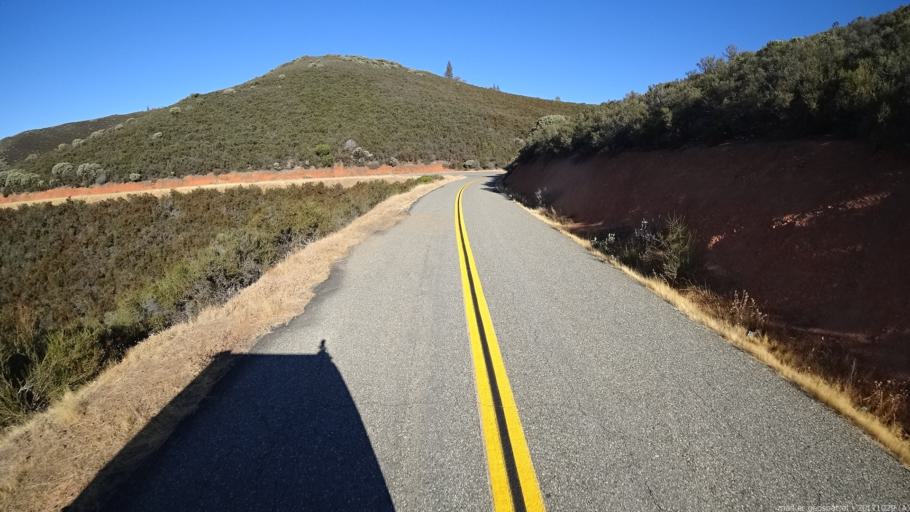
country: US
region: California
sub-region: Trinity County
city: Lewiston
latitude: 40.3651
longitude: -122.8510
